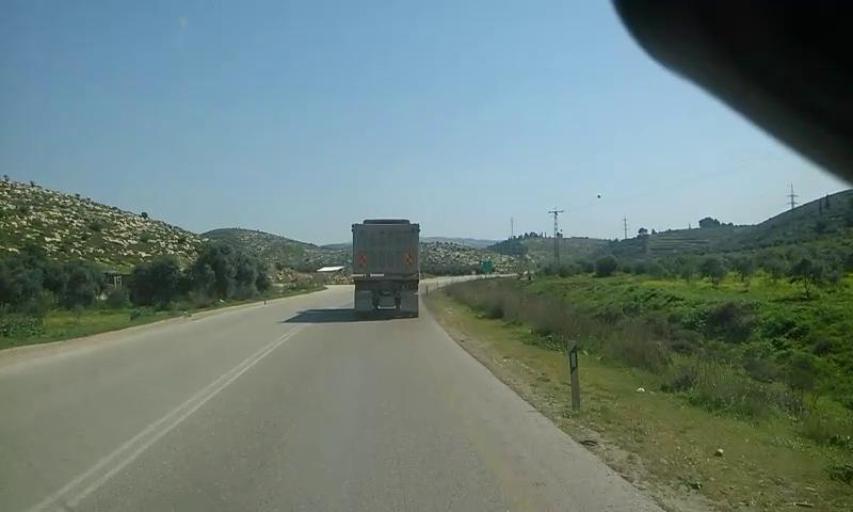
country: PS
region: West Bank
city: Idhna
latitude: 31.5864
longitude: 34.9725
